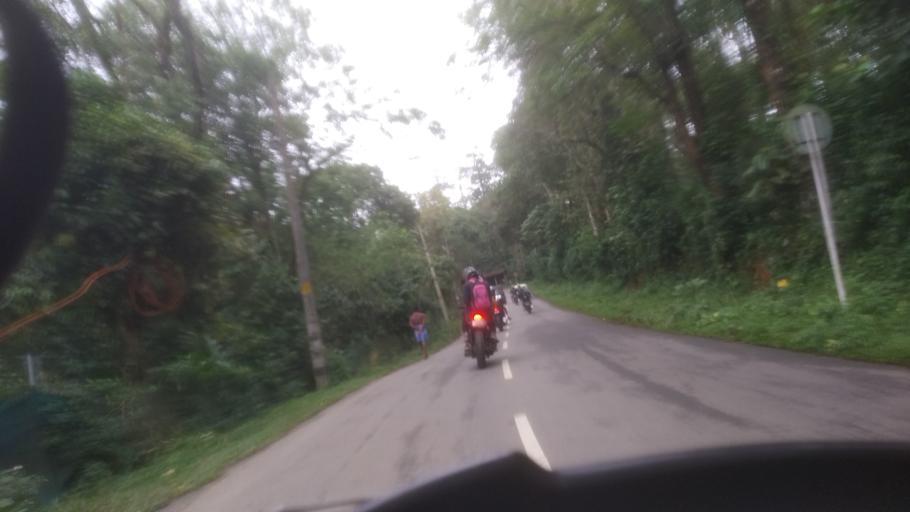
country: IN
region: Tamil Nadu
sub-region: Theni
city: Kombai
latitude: 9.8966
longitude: 77.1902
